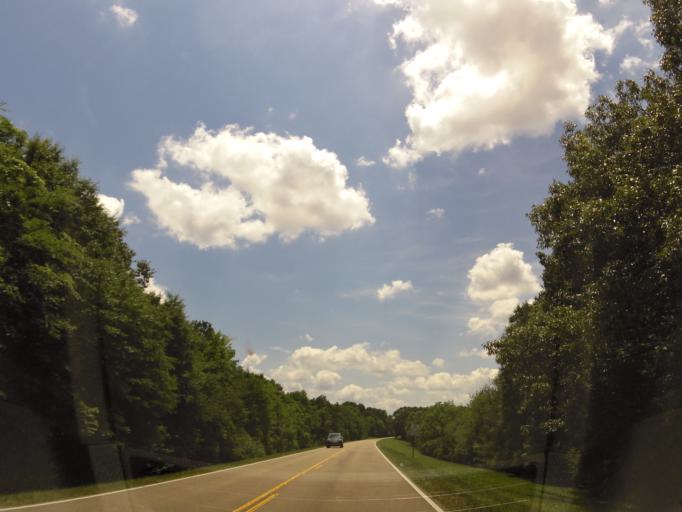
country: US
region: Mississippi
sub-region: Lee County
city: Tupelo
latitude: 34.2492
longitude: -88.7581
